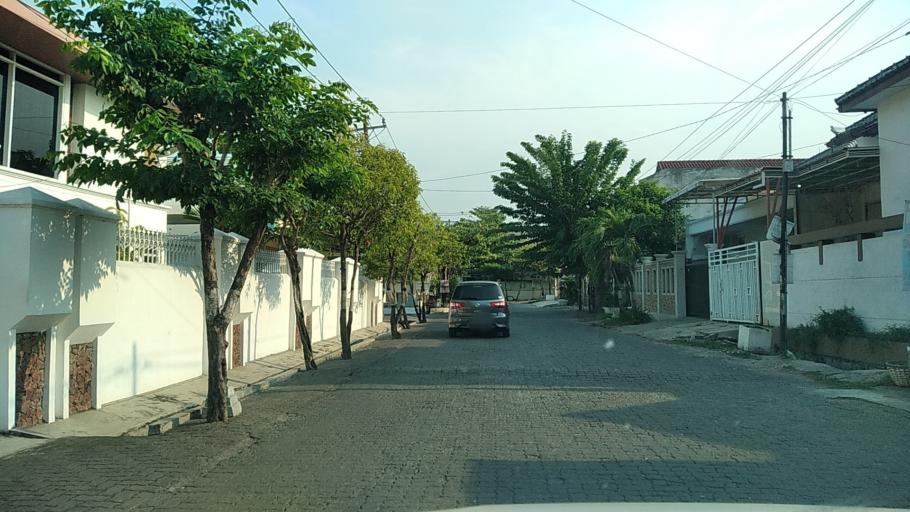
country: ID
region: Central Java
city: Semarang
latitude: -6.9632
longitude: 110.4053
